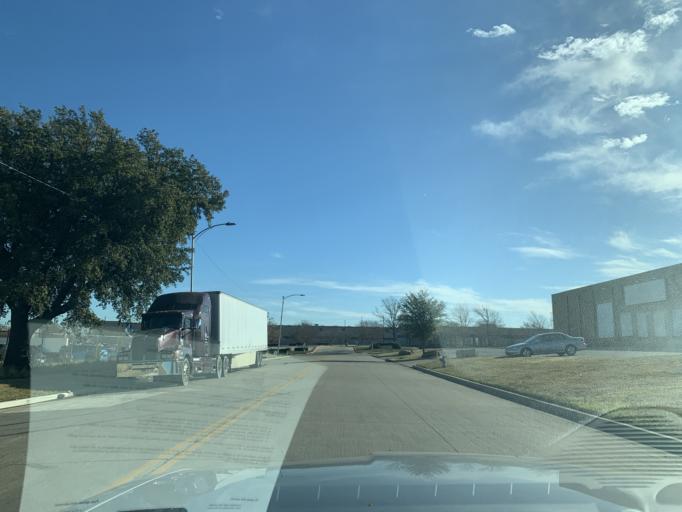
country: US
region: Texas
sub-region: Tarrant County
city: Arlington
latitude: 32.7445
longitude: -97.0700
